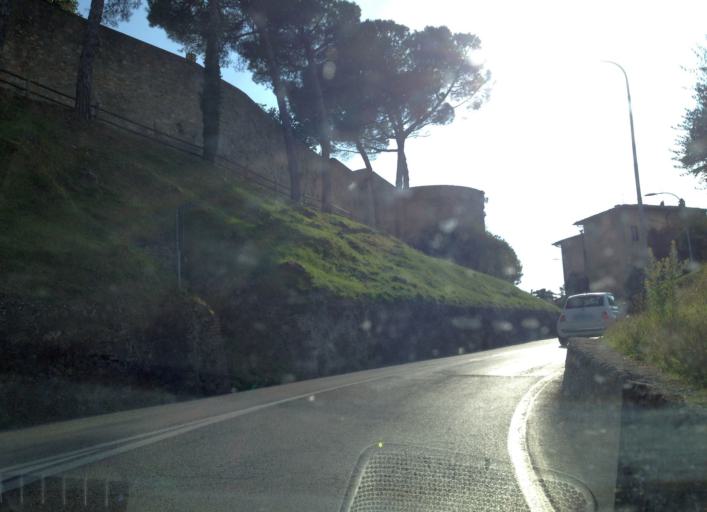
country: IT
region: Tuscany
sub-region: Provincia di Siena
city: San Gimignano
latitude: 43.4718
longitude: 11.0414
